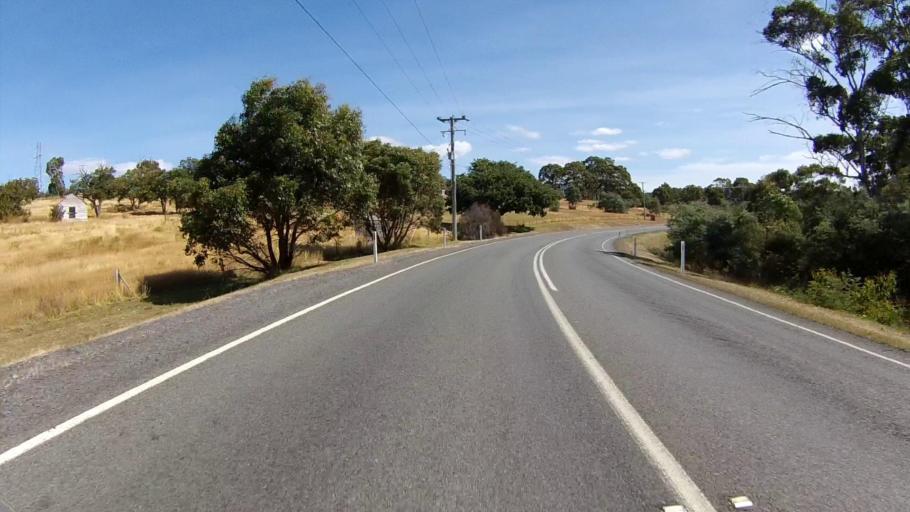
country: AU
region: Tasmania
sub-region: Sorell
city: Sorell
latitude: -42.6103
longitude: 147.7344
